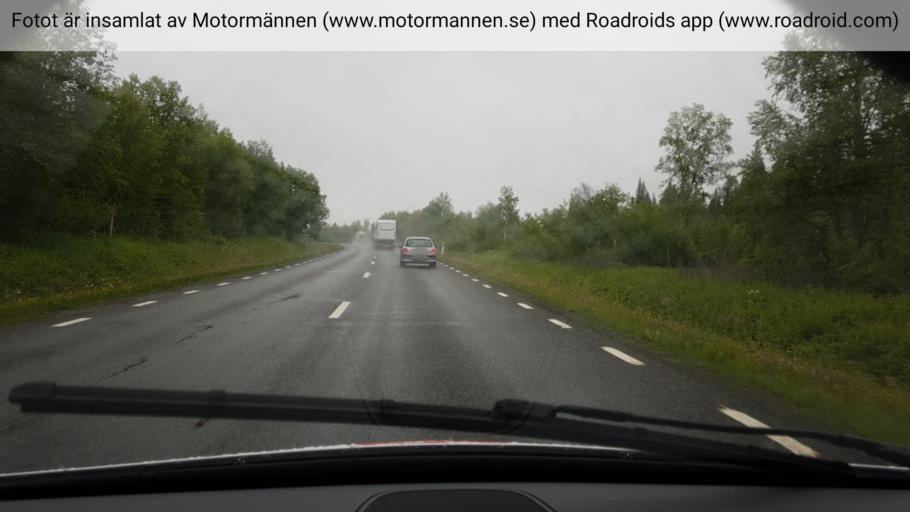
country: SE
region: Jaemtland
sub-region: OEstersunds Kommun
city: Lit
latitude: 63.4641
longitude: 15.1840
